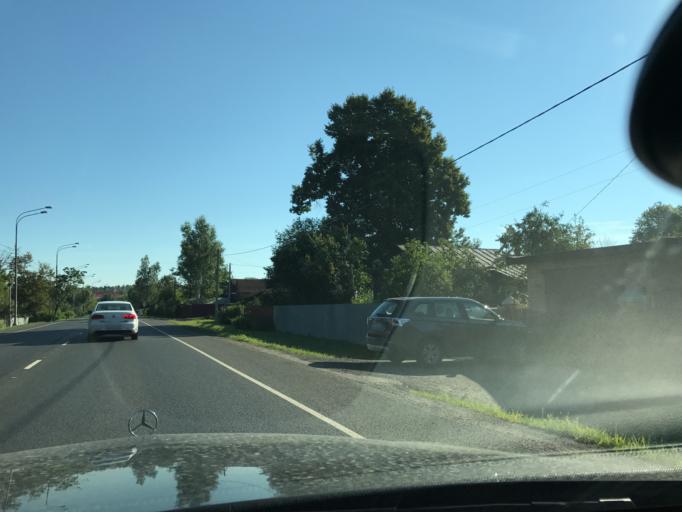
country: RU
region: Moskovskaya
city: Sverdlovskiy
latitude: 55.9235
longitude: 38.1329
